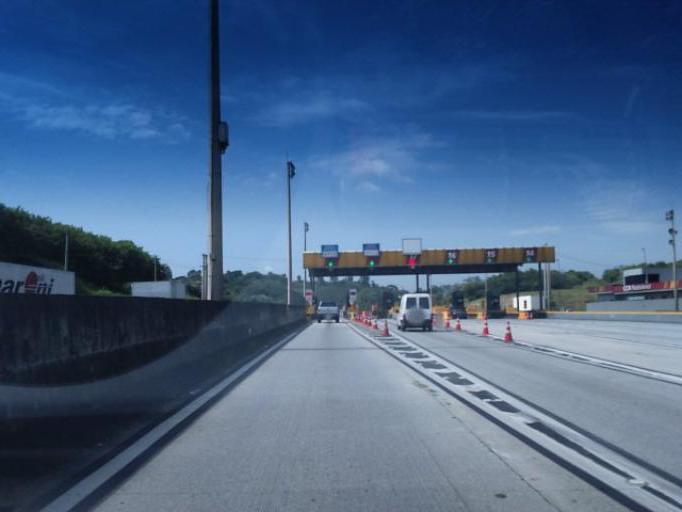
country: BR
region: Sao Paulo
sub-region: Taboao Da Serra
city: Taboao da Serra
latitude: -23.6014
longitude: -46.8128
